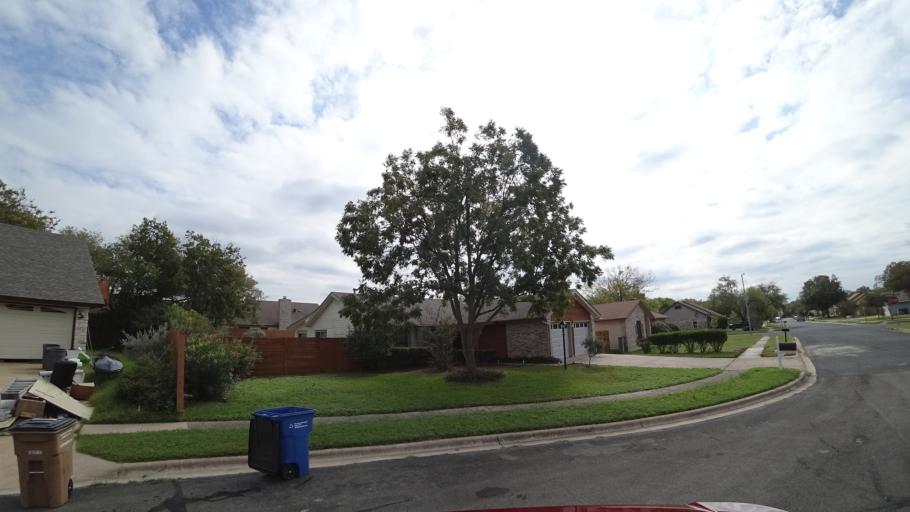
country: US
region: Texas
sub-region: Travis County
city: Wells Branch
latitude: 30.4243
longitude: -97.6924
